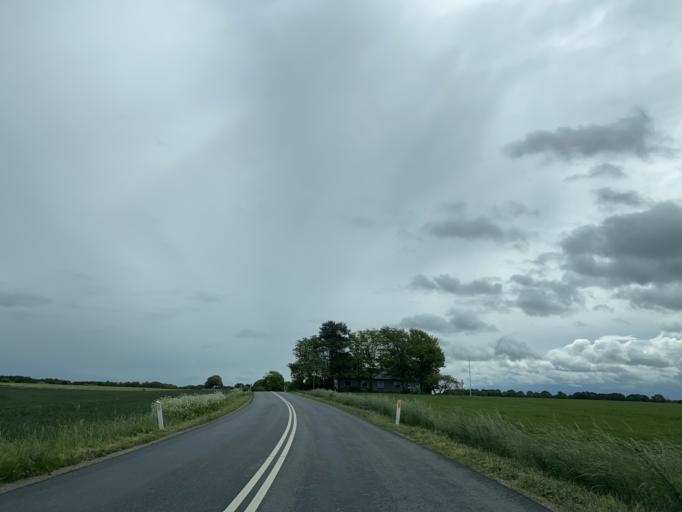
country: DK
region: Central Jutland
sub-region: Arhus Kommune
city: Sabro
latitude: 56.2499
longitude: 9.9943
